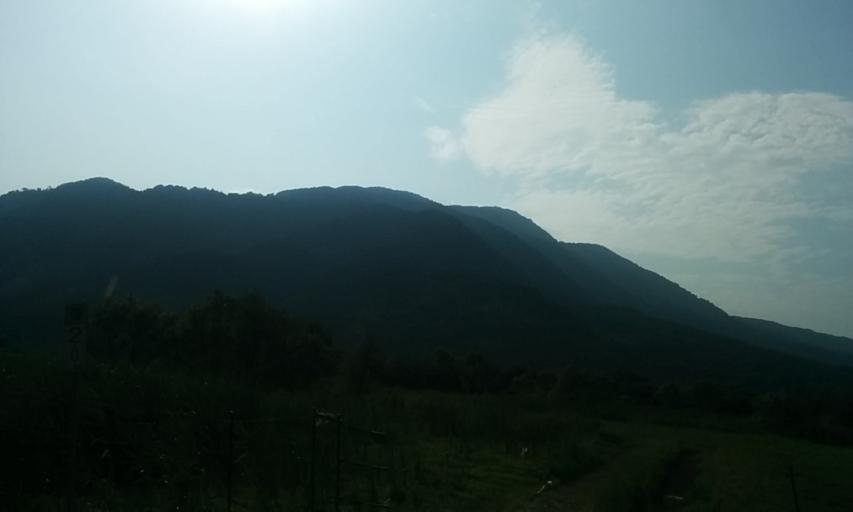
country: JP
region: Kyoto
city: Maizuru
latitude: 35.4953
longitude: 135.2911
